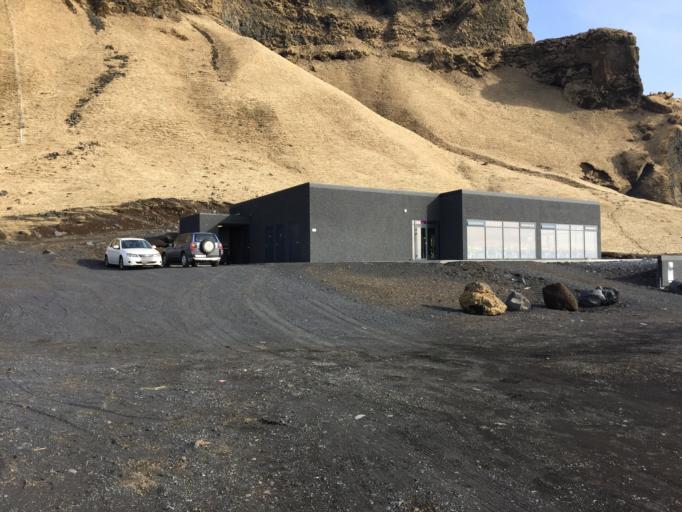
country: IS
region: South
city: Vestmannaeyjar
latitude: 63.4044
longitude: -19.0445
